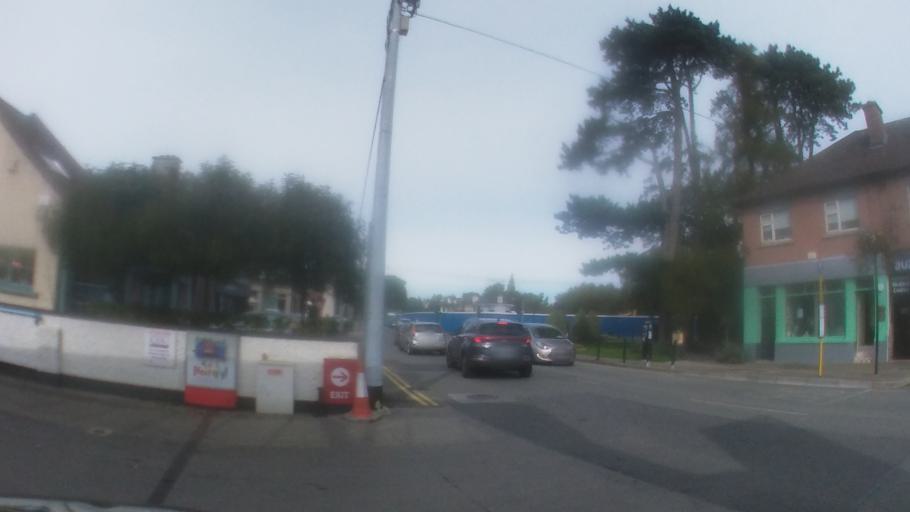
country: IE
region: Leinster
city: Foxrock
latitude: 53.2666
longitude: -6.1841
